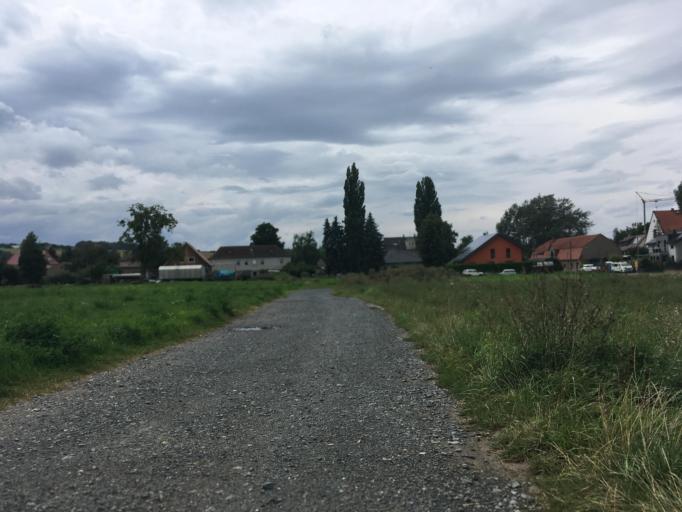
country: DE
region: Saxony
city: Dohna
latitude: 50.9372
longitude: 13.8941
